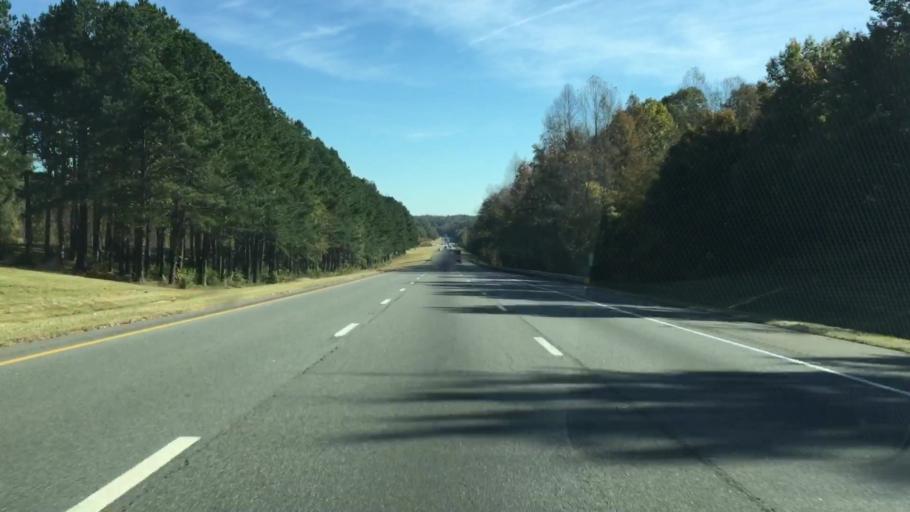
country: US
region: North Carolina
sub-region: Davidson County
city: Lexington
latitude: 35.7840
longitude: -80.2458
